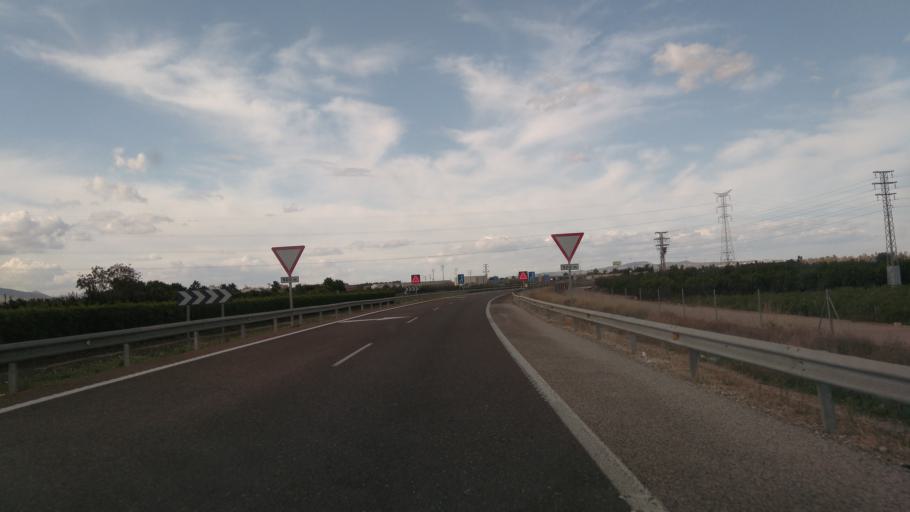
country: ES
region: Valencia
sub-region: Provincia de Valencia
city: L'Alcudia
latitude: 39.1873
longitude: -0.4918
